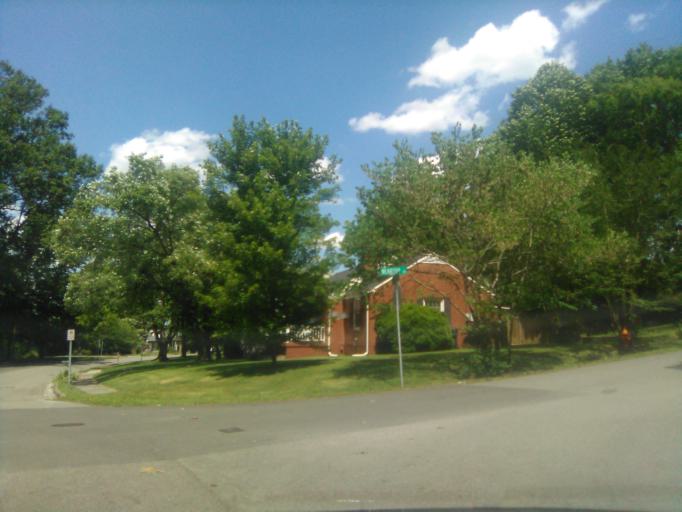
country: US
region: Tennessee
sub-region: Davidson County
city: Belle Meade
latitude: 36.1347
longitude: -86.8601
